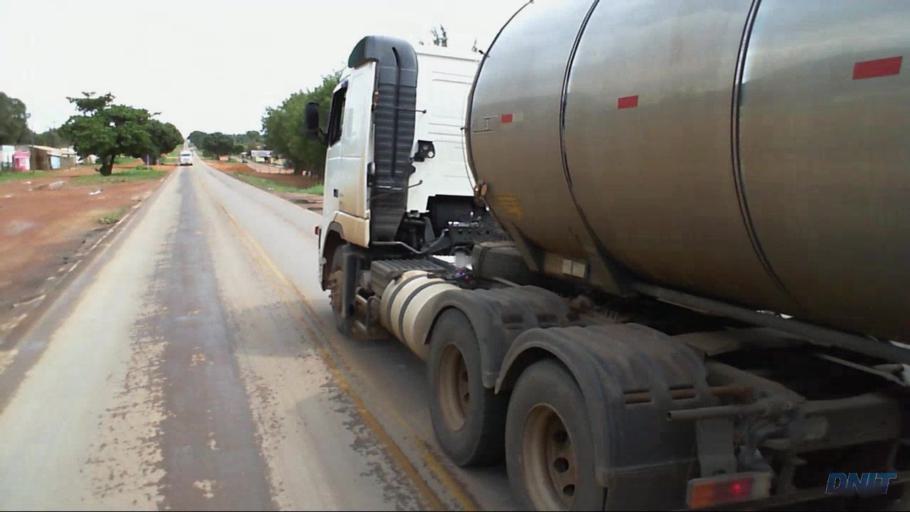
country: BR
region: Goias
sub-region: Padre Bernardo
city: Padre Bernardo
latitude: -15.2645
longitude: -48.2644
